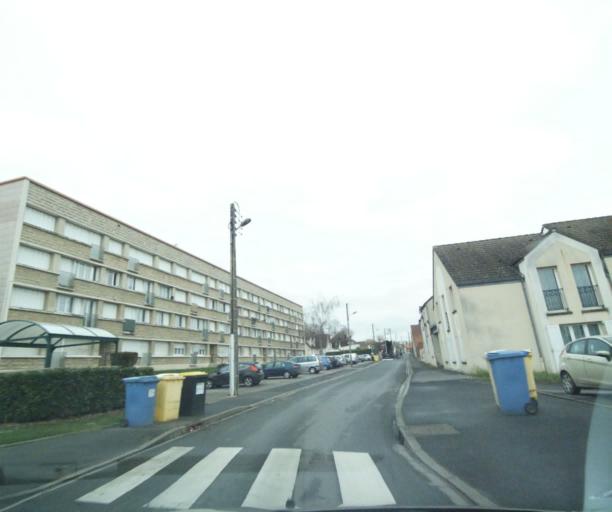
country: FR
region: Picardie
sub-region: Departement de l'Oise
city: Noyon
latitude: 49.5747
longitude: 2.9896
